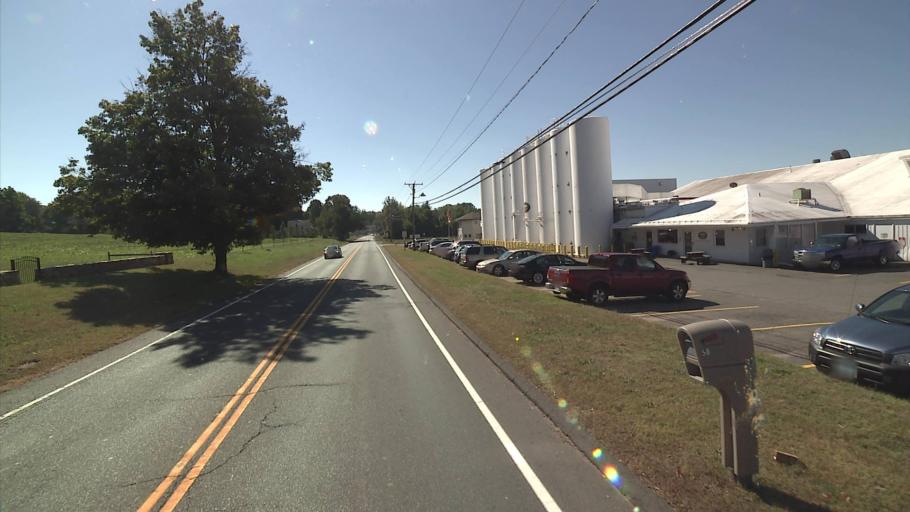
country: US
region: Connecticut
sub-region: Tolland County
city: Rockville
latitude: 41.8768
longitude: -72.4637
